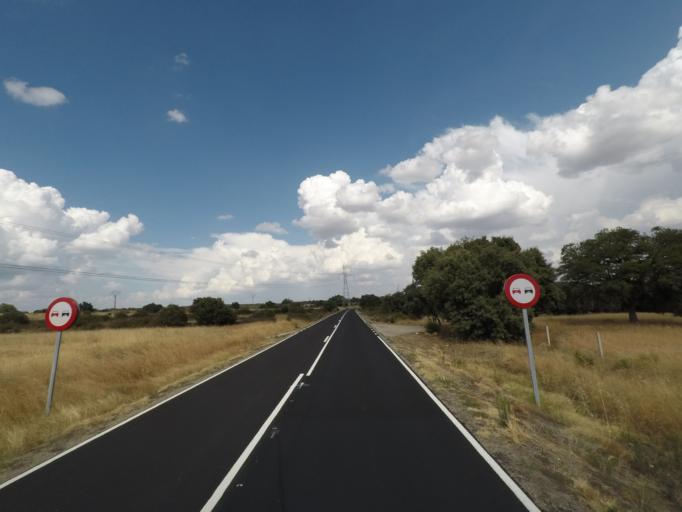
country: ES
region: Castille and Leon
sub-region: Provincia de Zamora
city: Fermoselle
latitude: 41.3004
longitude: -6.3266
